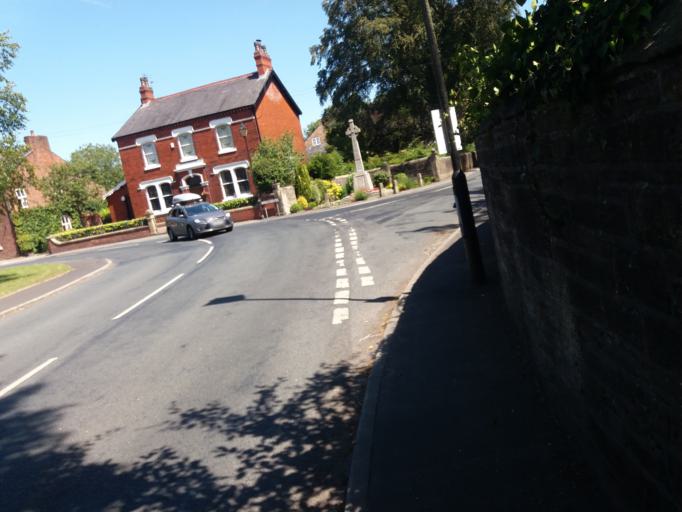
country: GB
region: England
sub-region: Lancashire
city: Croston
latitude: 53.6602
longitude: -2.7718
